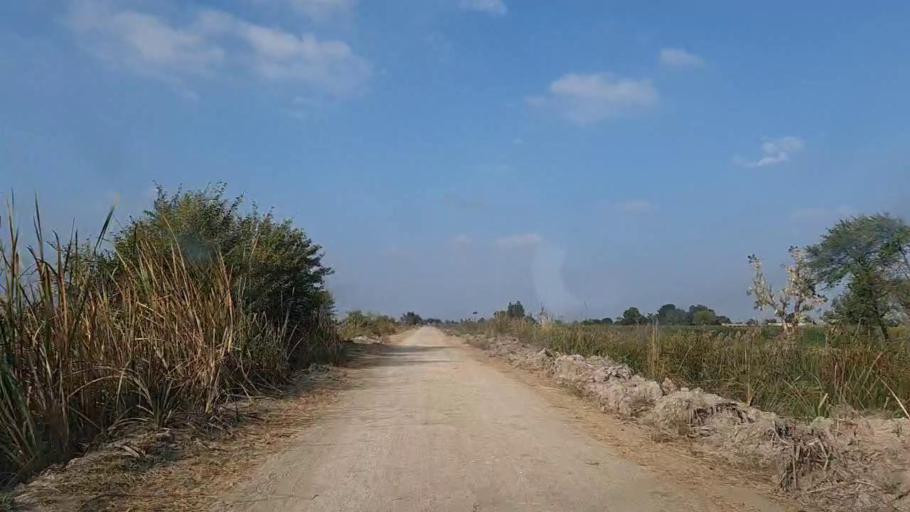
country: PK
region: Sindh
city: Sanghar
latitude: 26.2331
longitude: 68.9729
